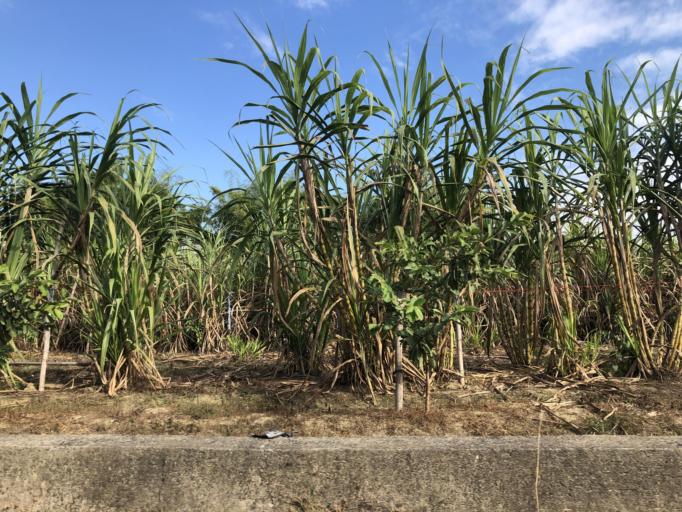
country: TW
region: Taiwan
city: Yujing
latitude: 23.0482
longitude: 120.4011
